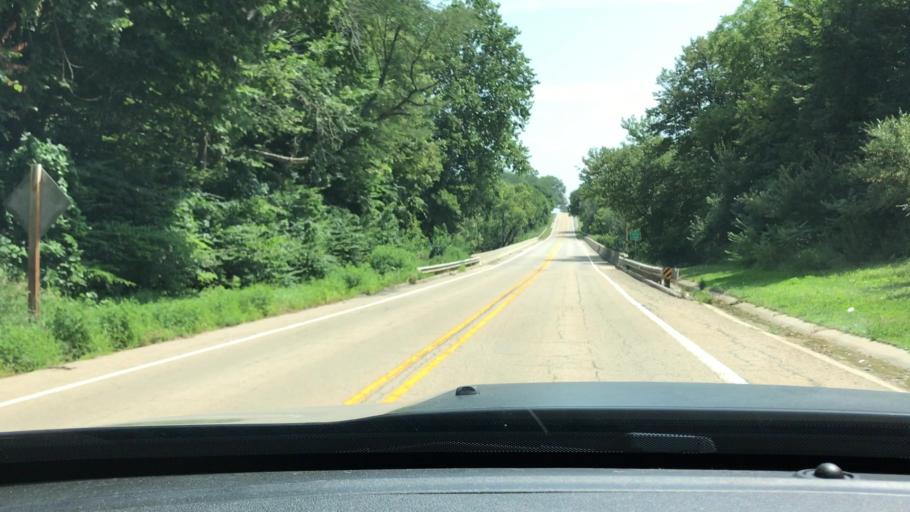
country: US
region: Illinois
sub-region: LaSalle County
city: Sheridan
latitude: 41.4852
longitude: -88.7752
